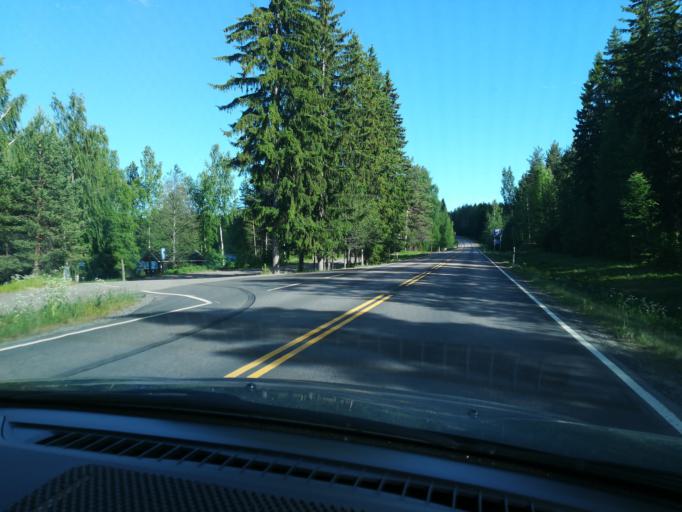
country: FI
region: Southern Savonia
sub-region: Mikkeli
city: Puumala
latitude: 61.5099
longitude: 28.1832
